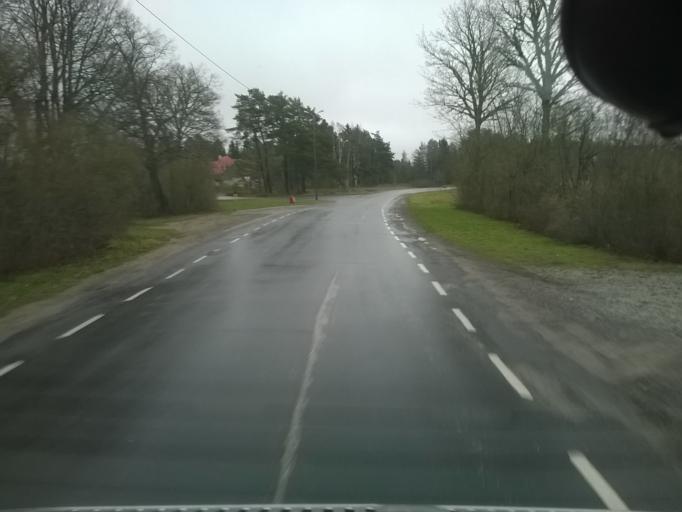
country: EE
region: Harju
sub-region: Nissi vald
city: Riisipere
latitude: 59.1115
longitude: 24.3131
